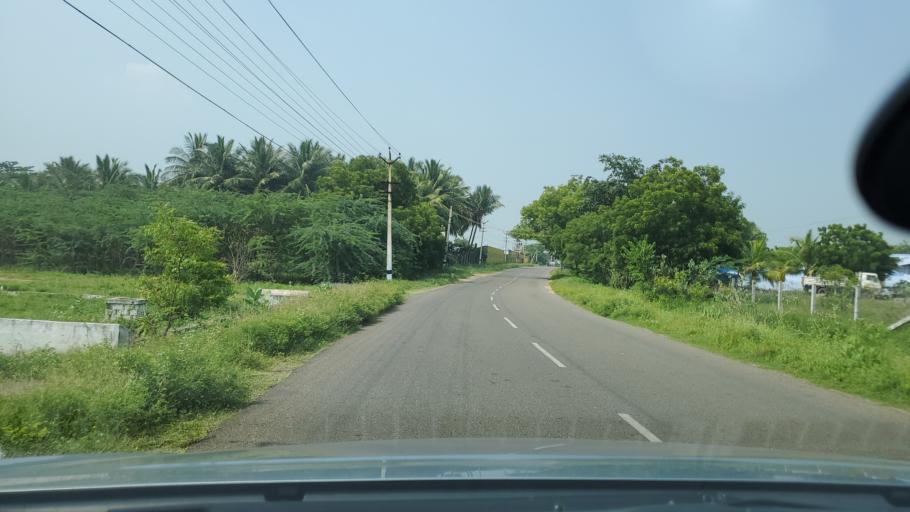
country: IN
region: Tamil Nadu
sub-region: Erode
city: Chennimalai
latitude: 11.1891
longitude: 77.6180
